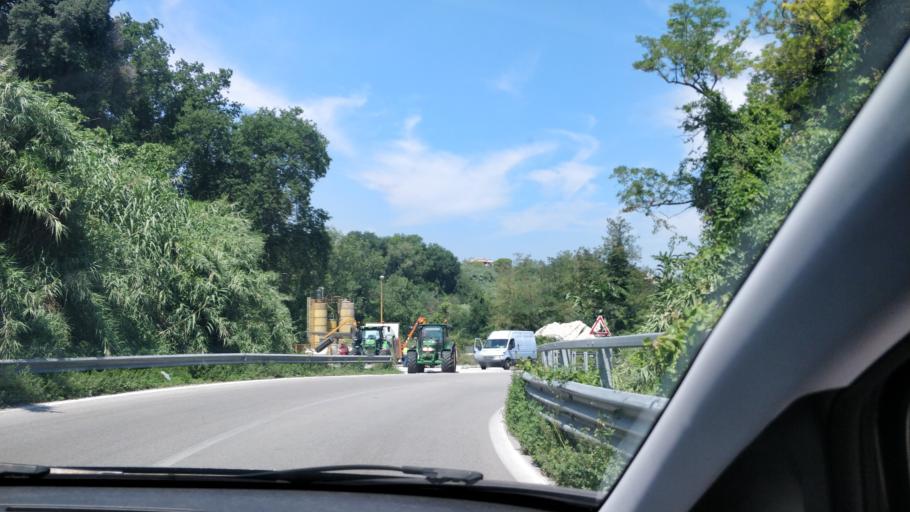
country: IT
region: Abruzzo
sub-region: Provincia di Chieti
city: Ortona
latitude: 42.3378
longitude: 14.4120
